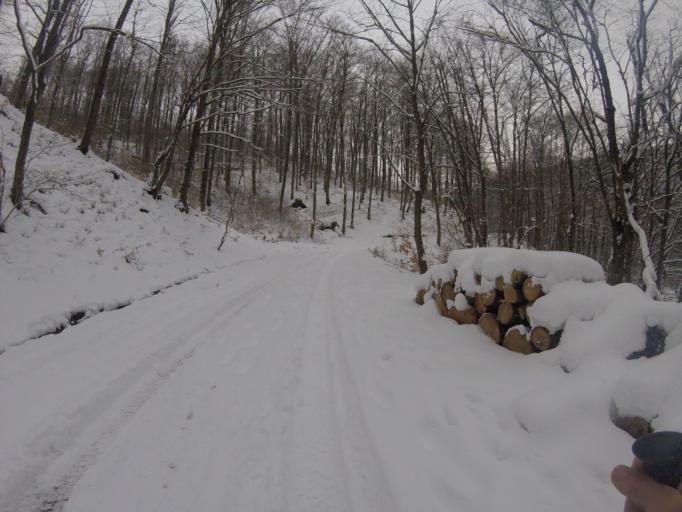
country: HU
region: Heves
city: Szilvasvarad
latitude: 48.0735
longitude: 20.4129
